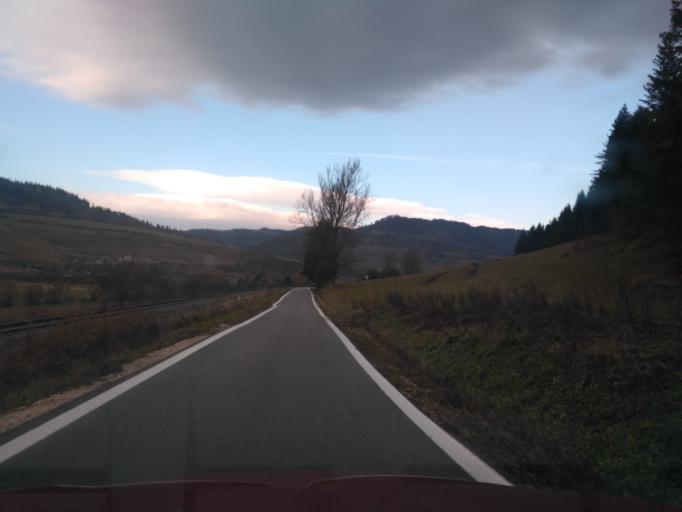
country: SK
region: Kosicky
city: Spisska Nova Ves
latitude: 48.8291
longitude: 20.6041
